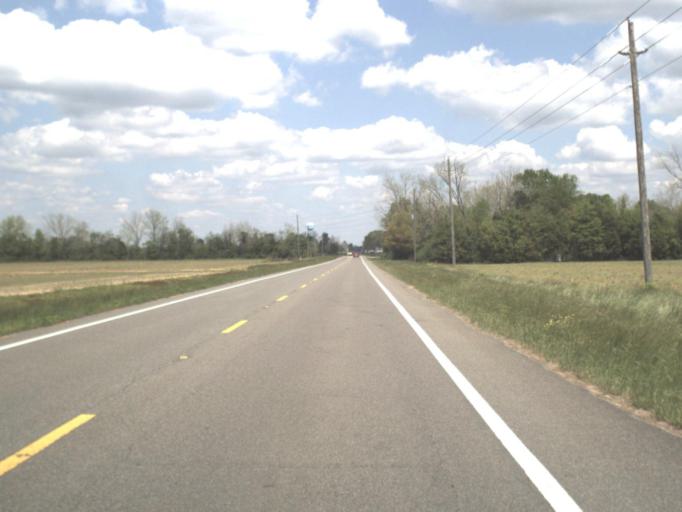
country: US
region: Florida
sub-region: Okaloosa County
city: Crestview
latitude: 30.8332
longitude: -86.6753
